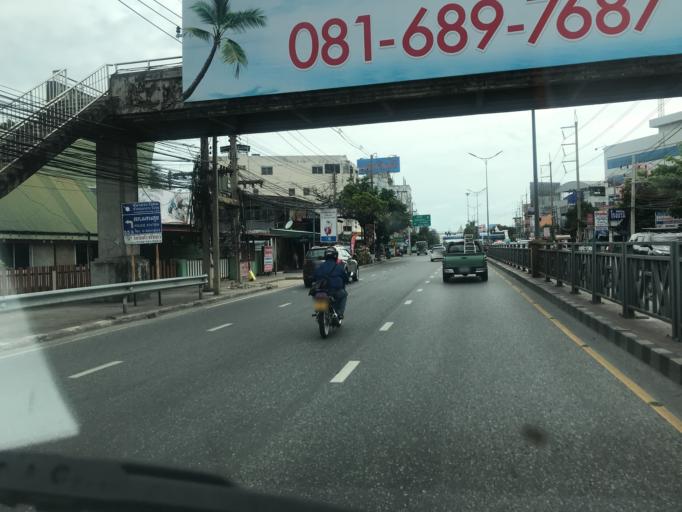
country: TH
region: Chon Buri
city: Chon Buri
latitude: 13.2849
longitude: 100.9381
